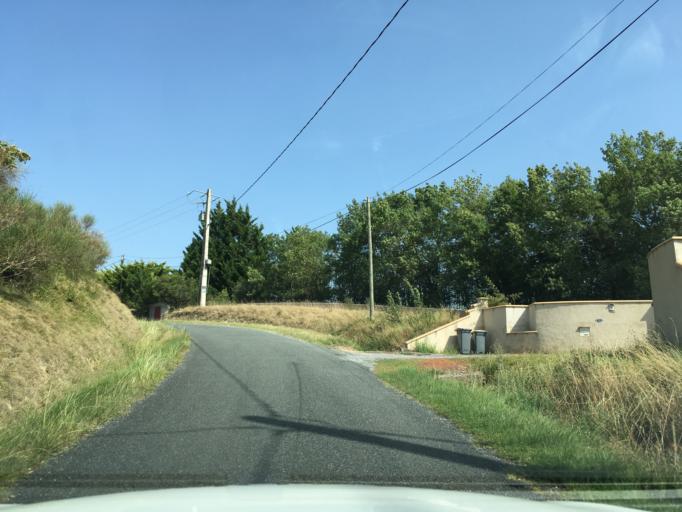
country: FR
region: Midi-Pyrenees
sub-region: Departement du Tarn
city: Lagarrigue
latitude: 43.5721
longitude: 2.2610
